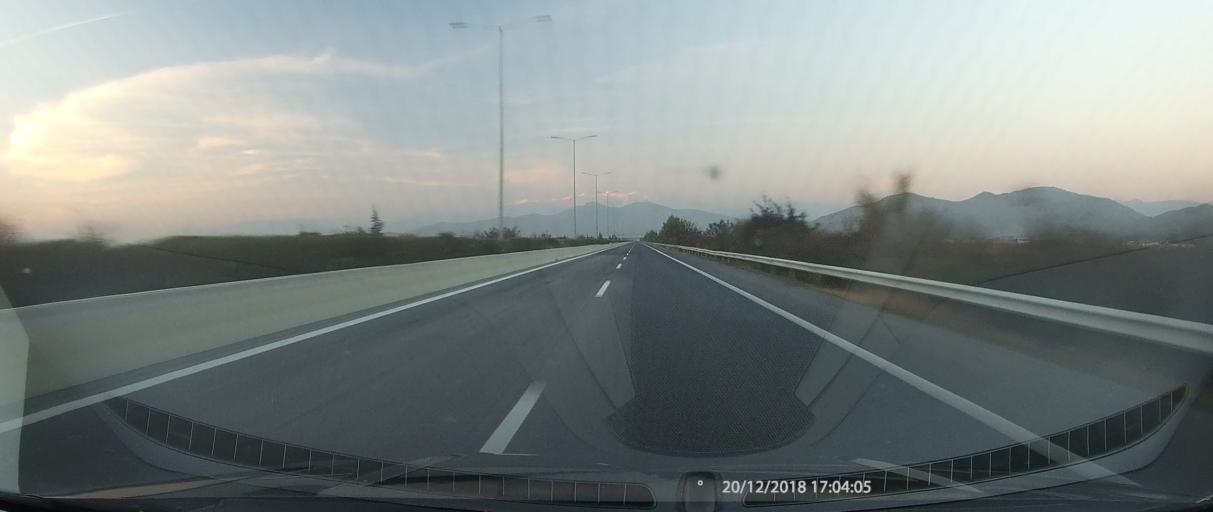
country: GR
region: Thessaly
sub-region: Nomos Larisis
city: Falani
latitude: 39.7103
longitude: 22.4841
